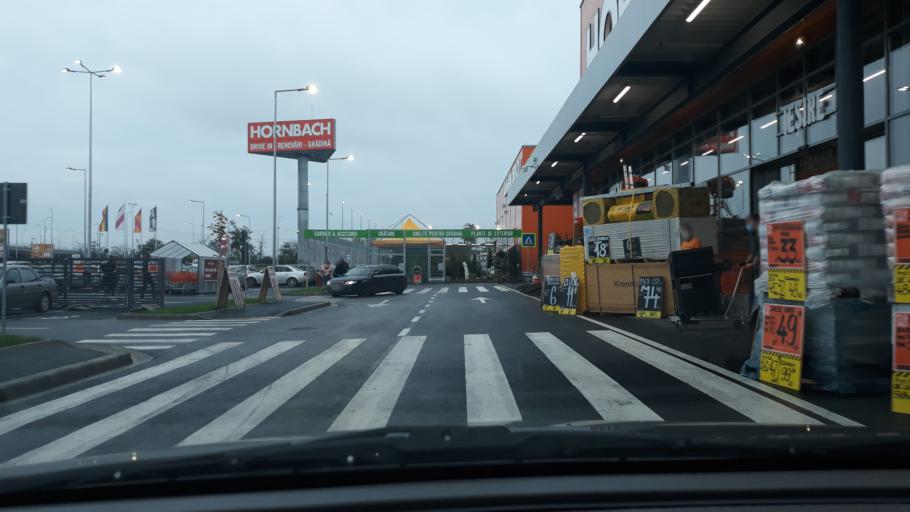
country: RO
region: Bihor
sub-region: Comuna Biharea
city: Oradea
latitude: 47.0452
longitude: 21.9005
